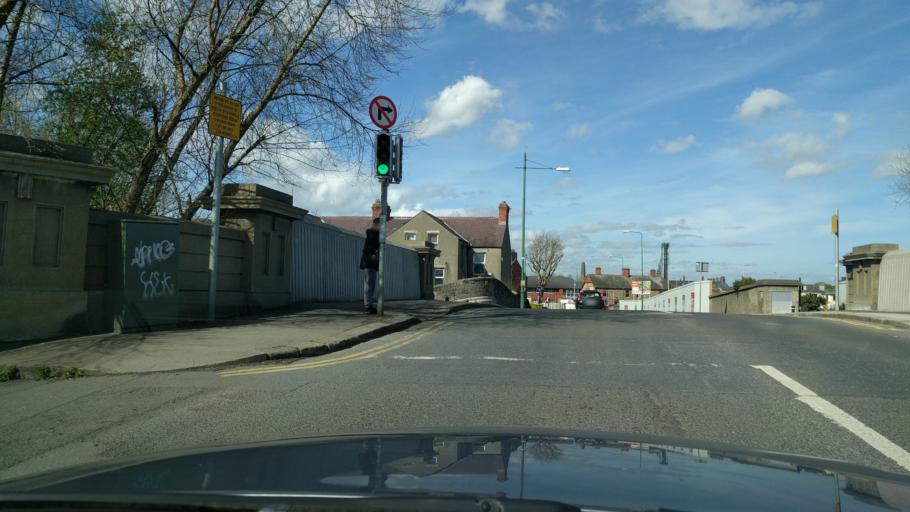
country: IE
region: Leinster
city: Rialto
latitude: 53.3375
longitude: -6.2993
